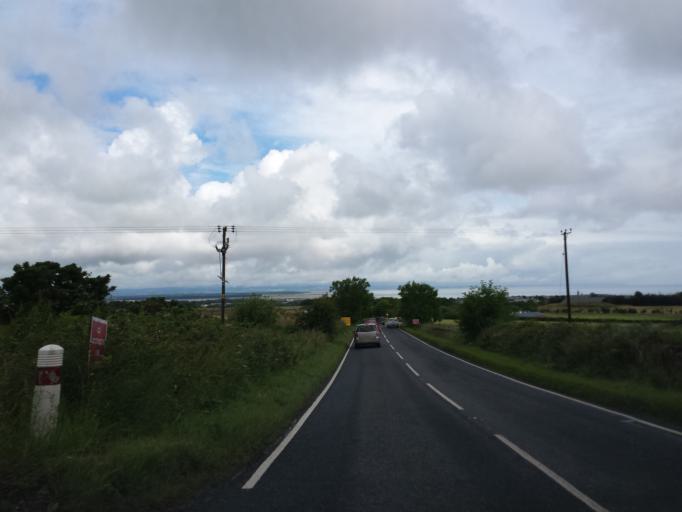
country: GB
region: Scotland
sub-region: Fife
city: Saint Andrews
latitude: 56.3118
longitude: -2.8230
